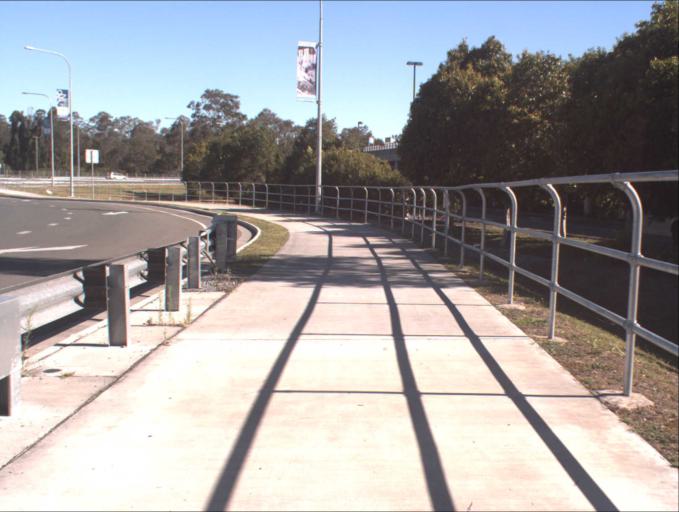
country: AU
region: Queensland
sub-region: Logan
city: Slacks Creek
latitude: -27.6381
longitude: 153.1365
